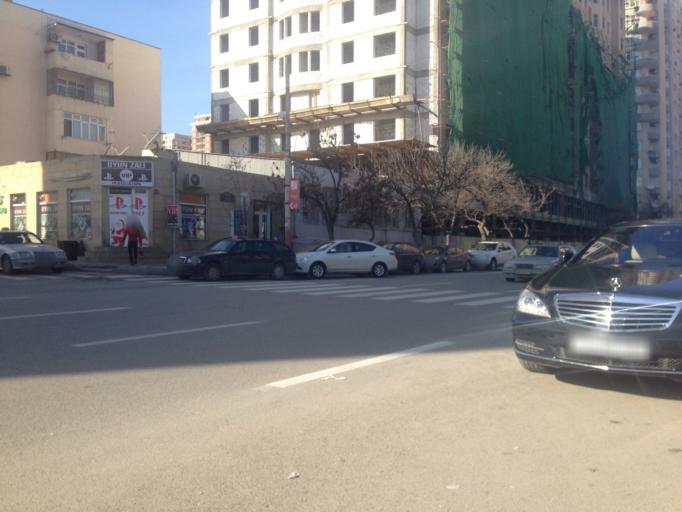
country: AZ
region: Baki
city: Baku
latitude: 40.3962
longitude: 49.8398
